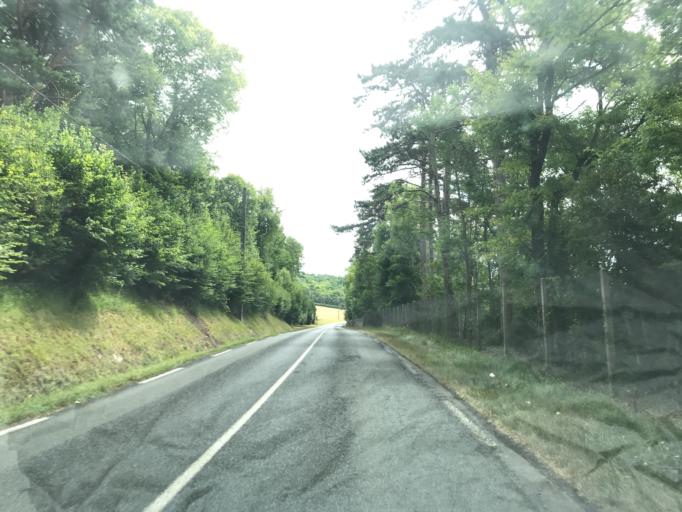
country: FR
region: Haute-Normandie
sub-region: Departement de l'Eure
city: Houlbec-Cocherel
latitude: 49.0627
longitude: 1.3252
